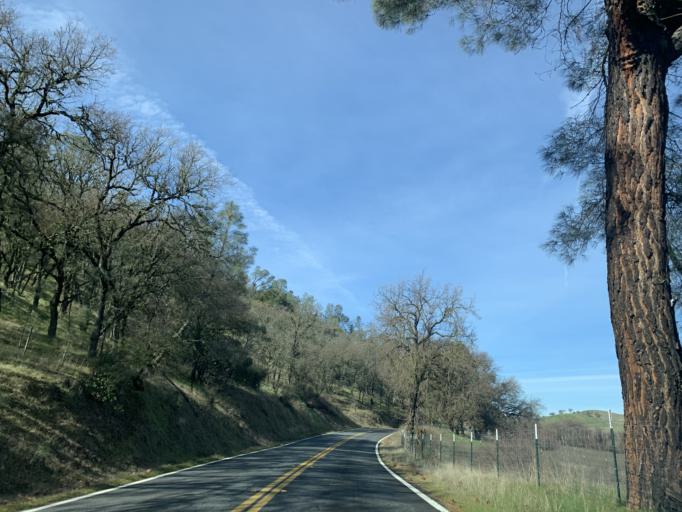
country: US
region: California
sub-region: Monterey County
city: Soledad
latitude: 36.5491
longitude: -121.1586
